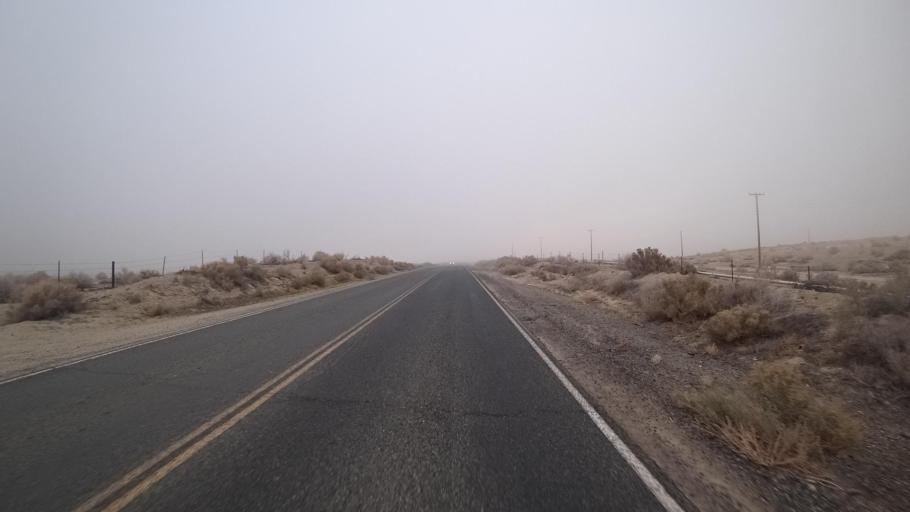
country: US
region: California
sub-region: Kern County
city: Ford City
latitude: 35.2738
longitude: -119.4676
